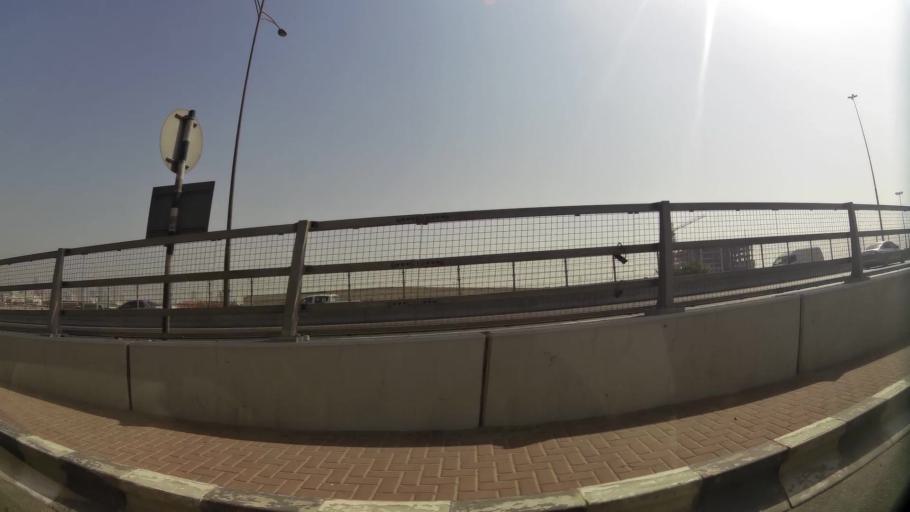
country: AE
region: Ash Shariqah
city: Sharjah
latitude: 25.2994
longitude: 55.3945
